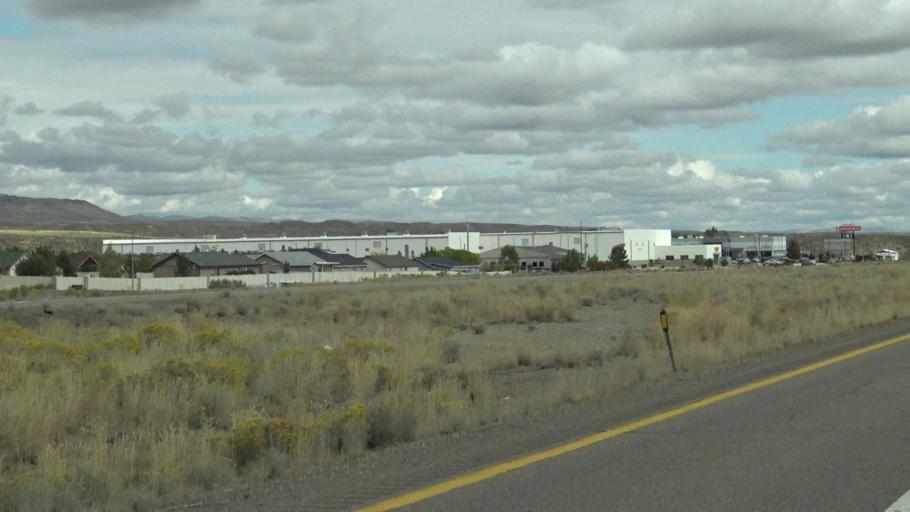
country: US
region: Nevada
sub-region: Elko County
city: Elko
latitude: 40.8622
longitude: -115.7361
